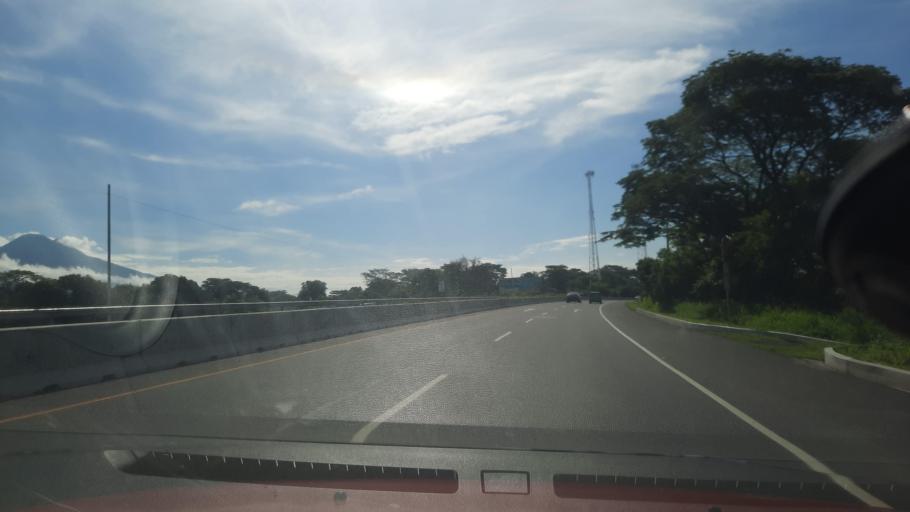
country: SV
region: La Paz
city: Santiago Nonualco
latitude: 13.4882
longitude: -88.9551
